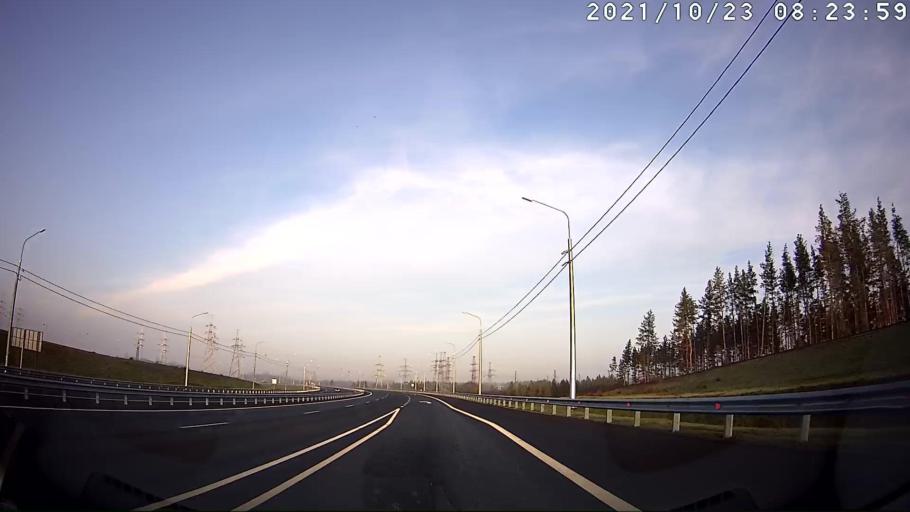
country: RU
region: Saratov
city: Sennoy
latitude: 52.1436
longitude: 46.9142
